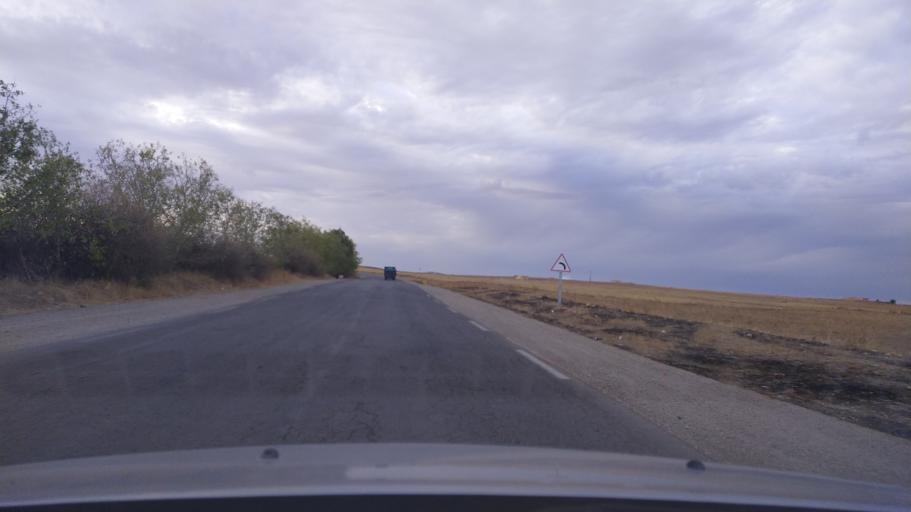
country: DZ
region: Tiaret
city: Frenda
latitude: 34.9843
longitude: 1.1416
